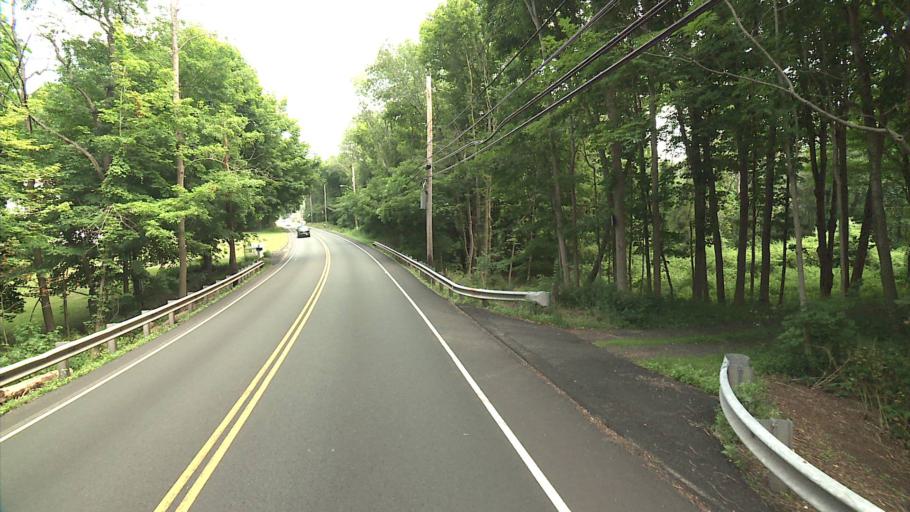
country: US
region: Connecticut
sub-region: New Haven County
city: North Branford
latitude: 41.3882
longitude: -72.7929
